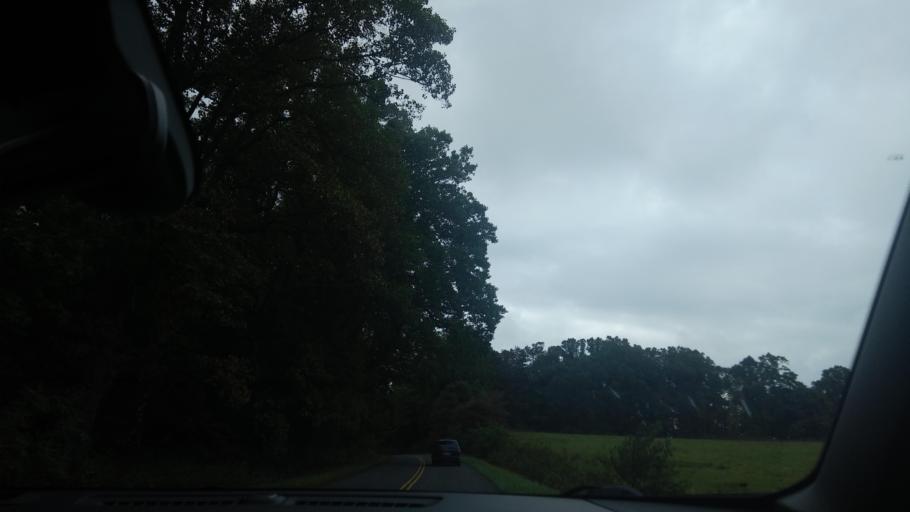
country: US
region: Virginia
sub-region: Carroll County
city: Cana
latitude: 36.6612
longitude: -80.6004
